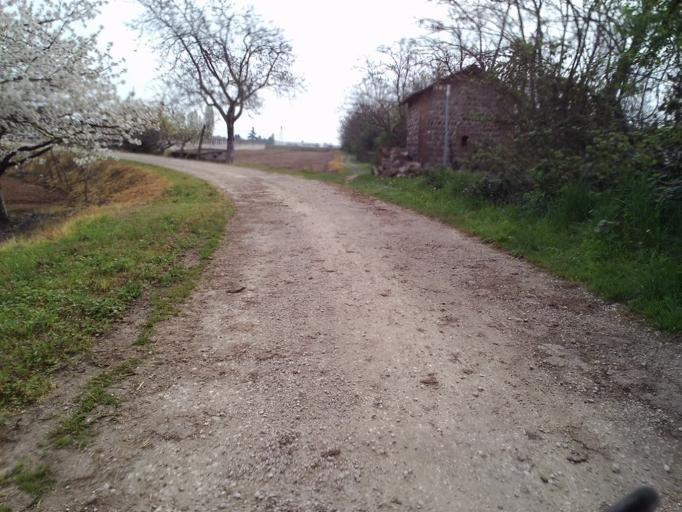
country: IT
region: Veneto
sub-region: Provincia di Verona
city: Rosegaferro
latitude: 45.3604
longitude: 10.7961
